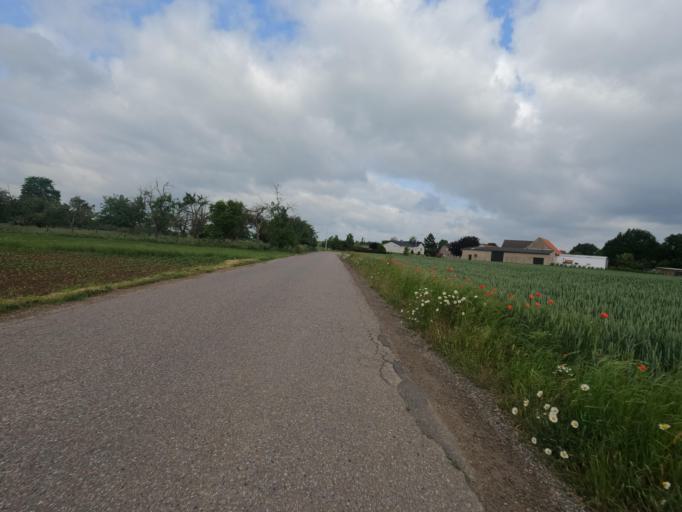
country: DE
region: North Rhine-Westphalia
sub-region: Regierungsbezirk Koln
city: Wassenberg
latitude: 51.0860
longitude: 6.1257
